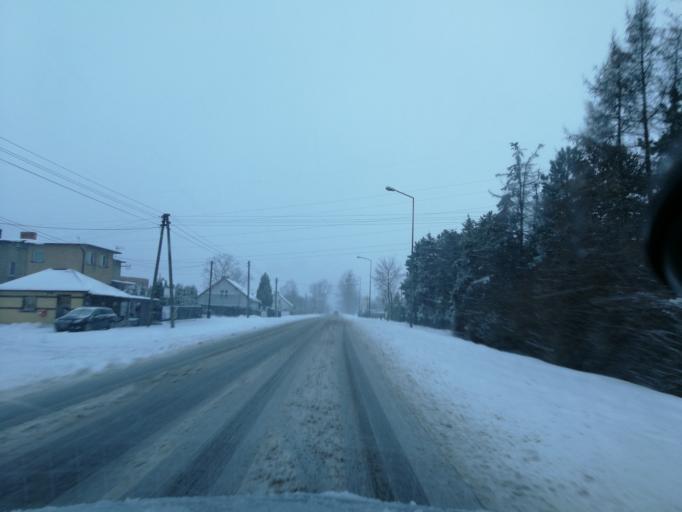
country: PL
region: Silesian Voivodeship
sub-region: Powiat pszczynski
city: Czarkow
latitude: 49.9920
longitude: 18.9092
